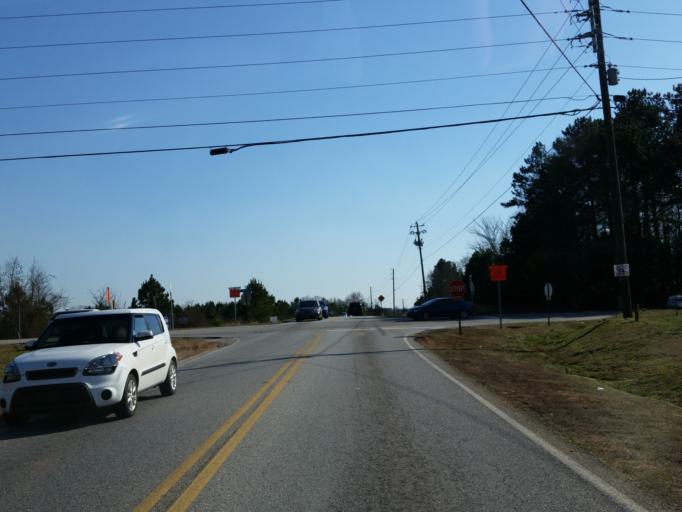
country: US
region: Georgia
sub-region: Henry County
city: McDonough
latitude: 33.4483
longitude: -84.2143
